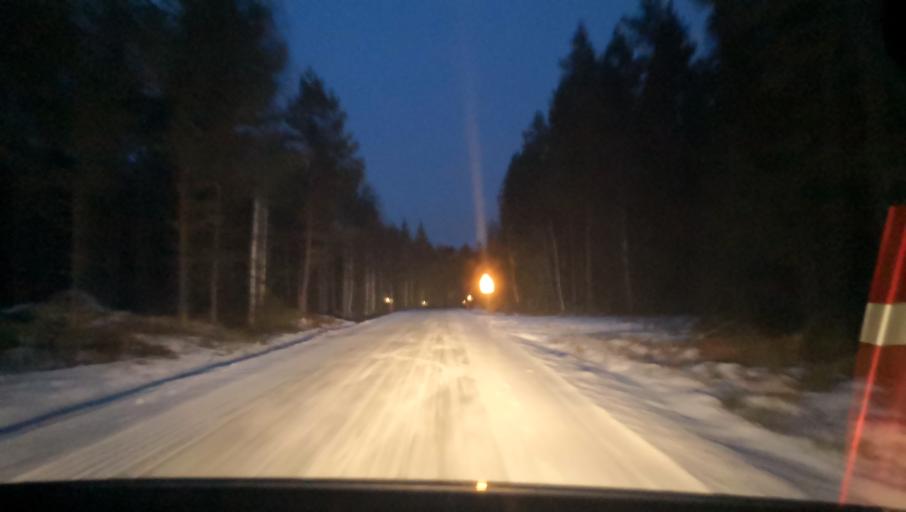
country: SE
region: Uppsala
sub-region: Heby Kommun
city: Tarnsjo
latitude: 60.2513
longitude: 16.7326
